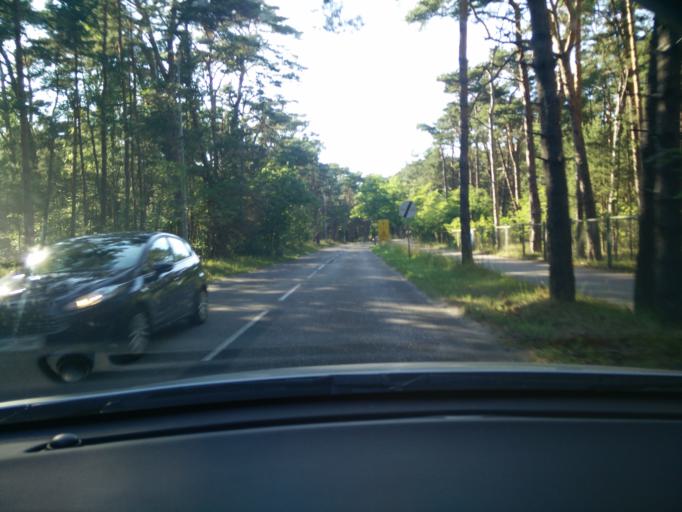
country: PL
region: Pomeranian Voivodeship
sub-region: Powiat pucki
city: Jastarnia
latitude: 54.6741
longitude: 18.7281
